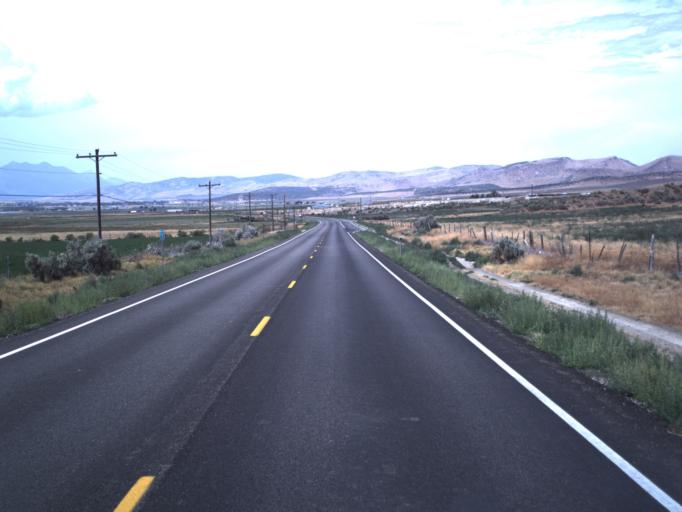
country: US
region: Utah
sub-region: Sanpete County
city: Moroni
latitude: 39.5537
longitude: -111.6002
